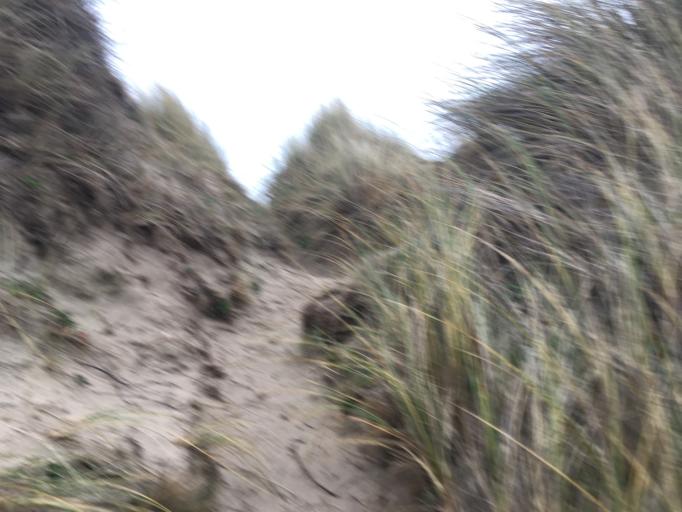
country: IE
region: Leinster
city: Portmarnock
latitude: 53.4195
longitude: -6.1217
